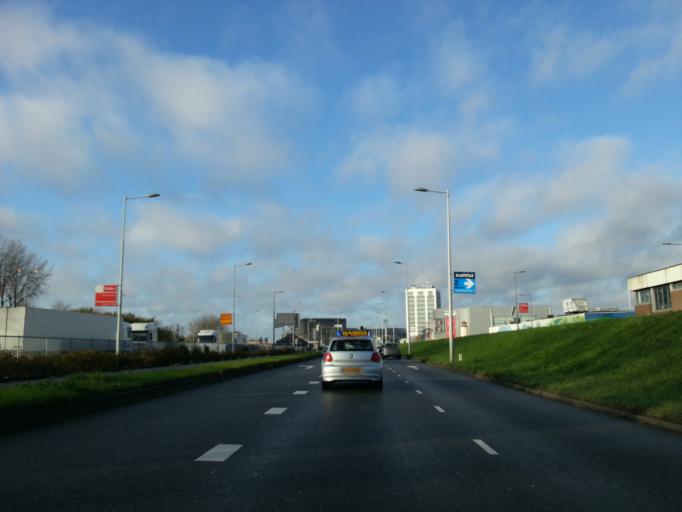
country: NL
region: South Holland
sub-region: Gemeente Rotterdam
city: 's-Gravenland
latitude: 51.8958
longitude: 4.5365
